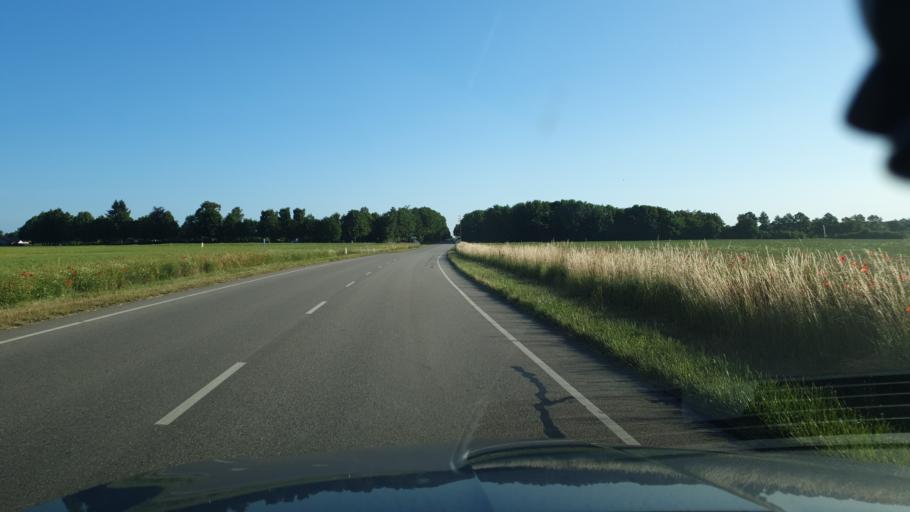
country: DK
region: Zealand
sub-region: Soro Kommune
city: Frederiksberg
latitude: 55.4044
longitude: 11.5636
